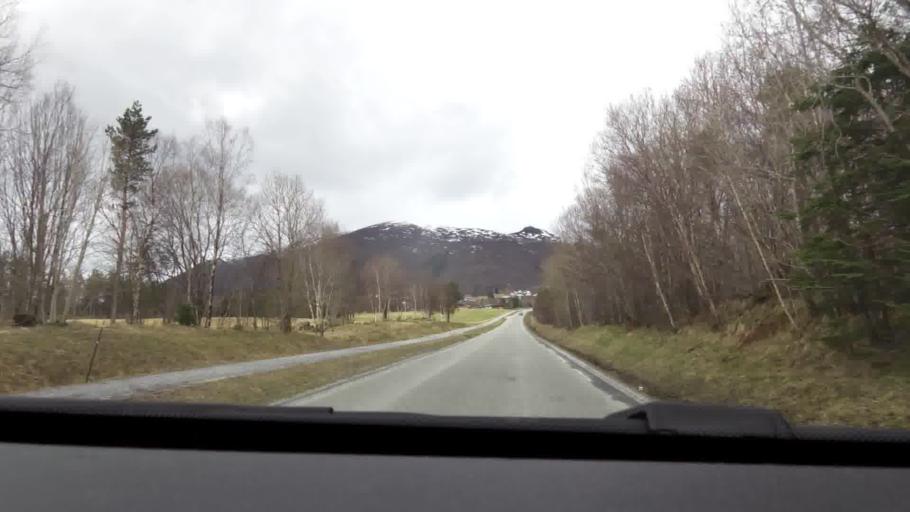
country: NO
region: More og Romsdal
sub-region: Eide
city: Eide
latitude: 62.9073
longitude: 7.4455
